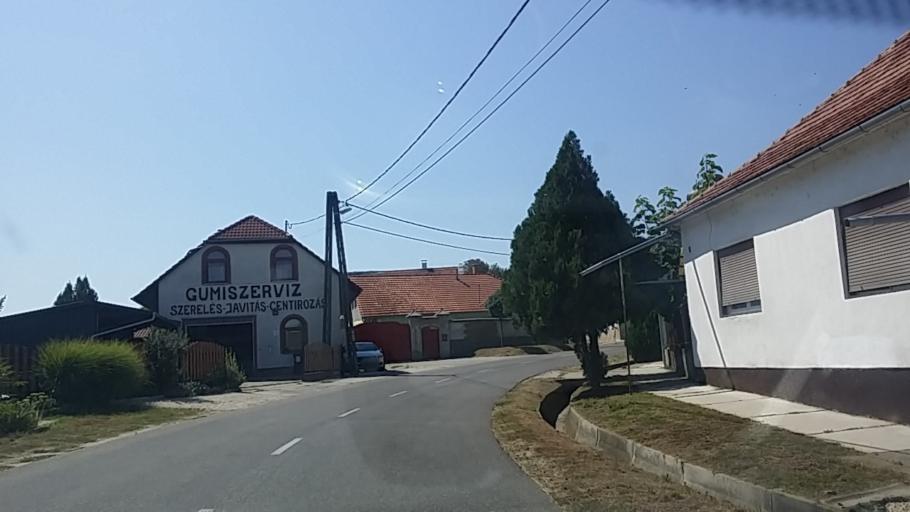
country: HU
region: Tolna
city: Paks
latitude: 46.6649
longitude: 18.8799
